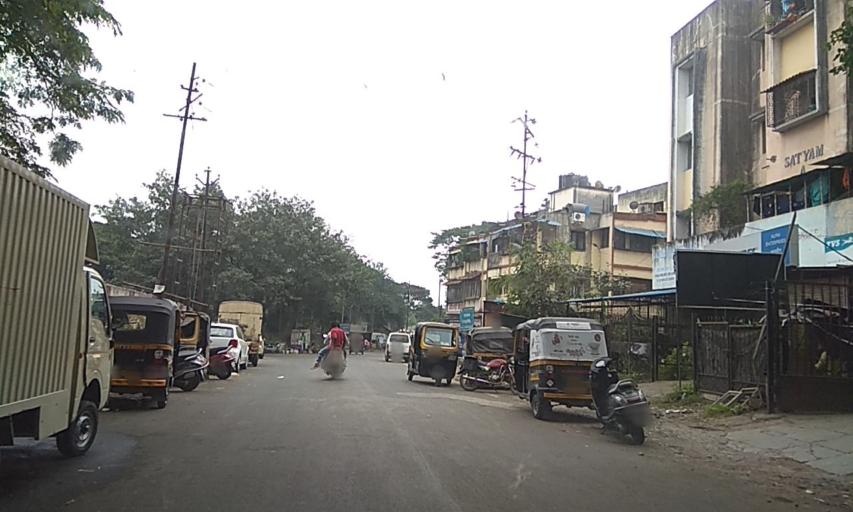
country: IN
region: Maharashtra
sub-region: Pune Division
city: Khadki
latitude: 18.5516
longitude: 73.8552
